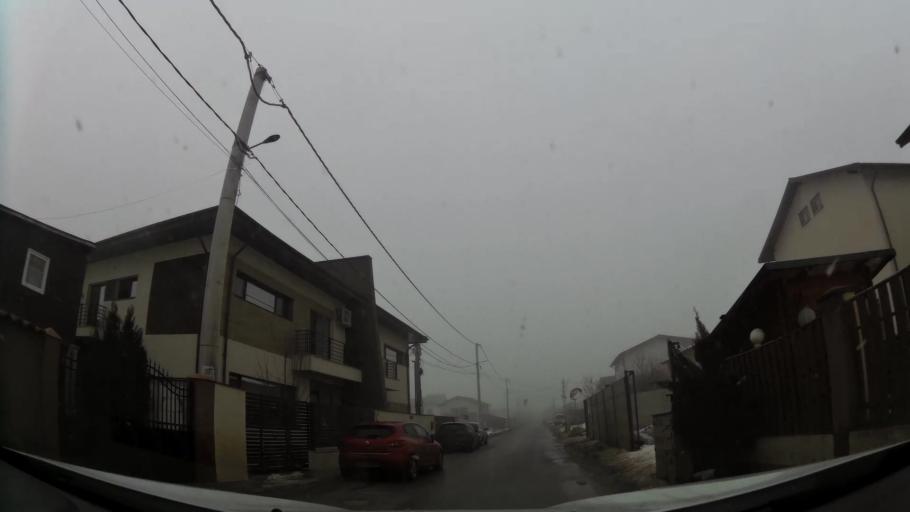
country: RO
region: Ilfov
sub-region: Comuna Chiajna
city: Chiajna
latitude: 44.4528
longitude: 25.9742
